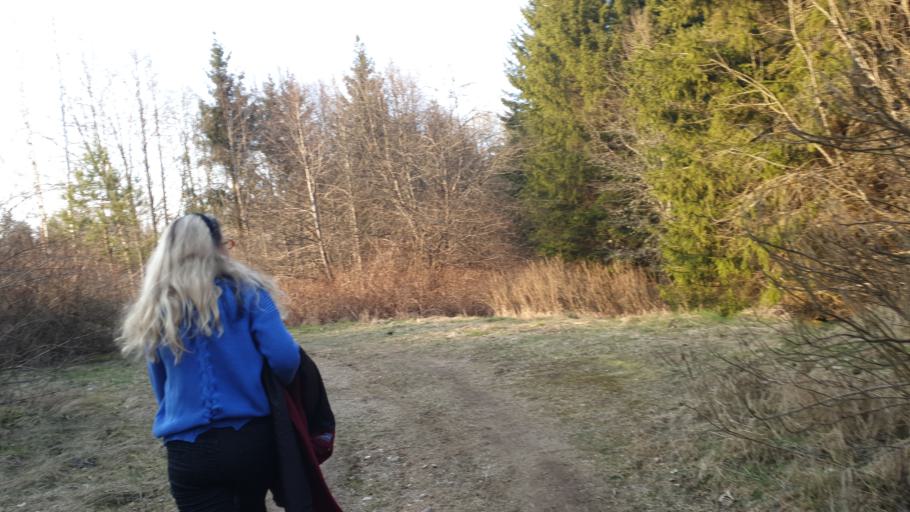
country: LT
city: Nemencine
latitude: 54.8759
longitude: 25.5761
